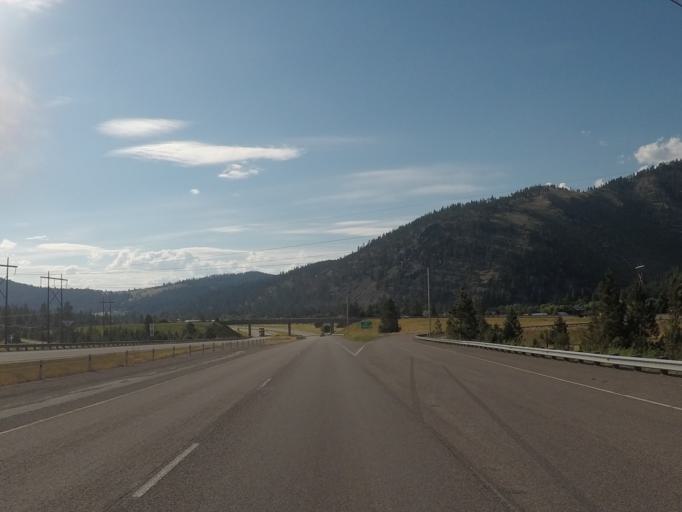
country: US
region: Montana
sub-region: Missoula County
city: Bonner-West Riverside
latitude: 46.8748
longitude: -113.8907
